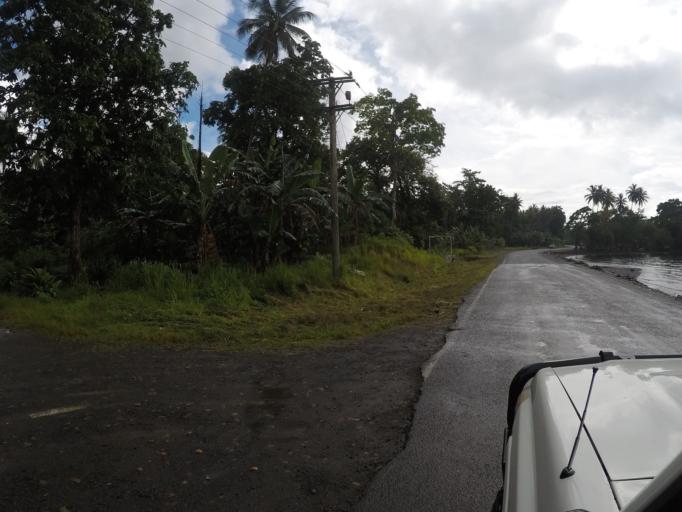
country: PG
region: Milne Bay
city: Alotau
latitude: -10.3224
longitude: 150.4845
